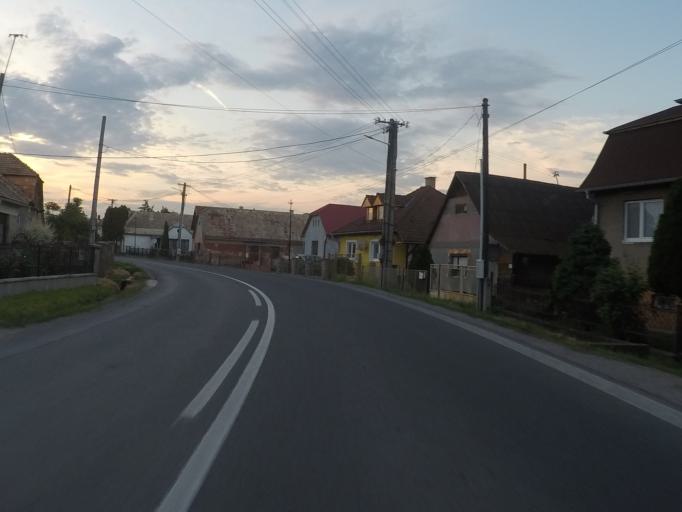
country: SK
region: Banskobystricky
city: Rimavska Sobota
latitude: 48.4509
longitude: 19.9595
